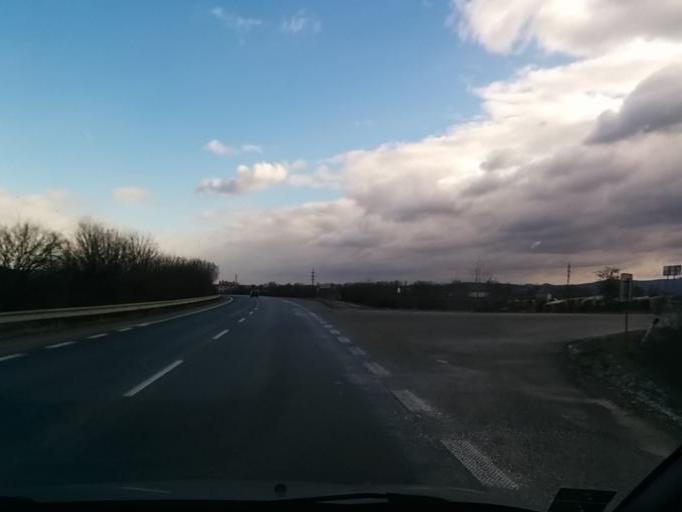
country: SK
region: Trenciansky
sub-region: Okres Trencin
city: Trencin
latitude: 48.8665
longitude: 17.9623
